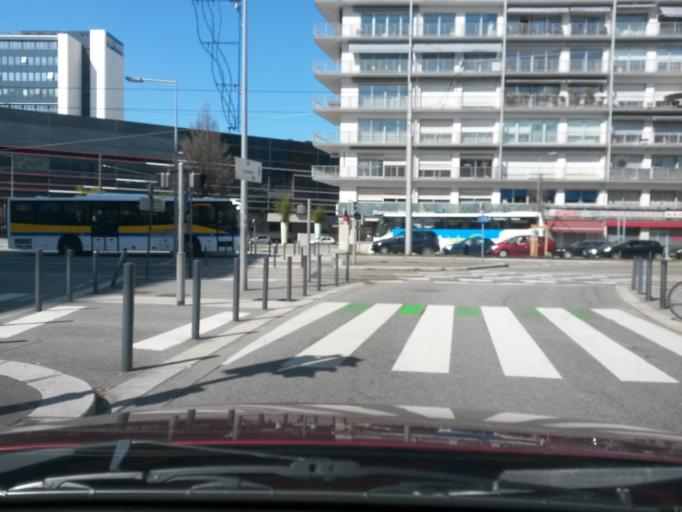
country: FR
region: Rhone-Alpes
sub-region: Departement de l'Isere
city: La Tronche
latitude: 45.1852
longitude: 5.7325
